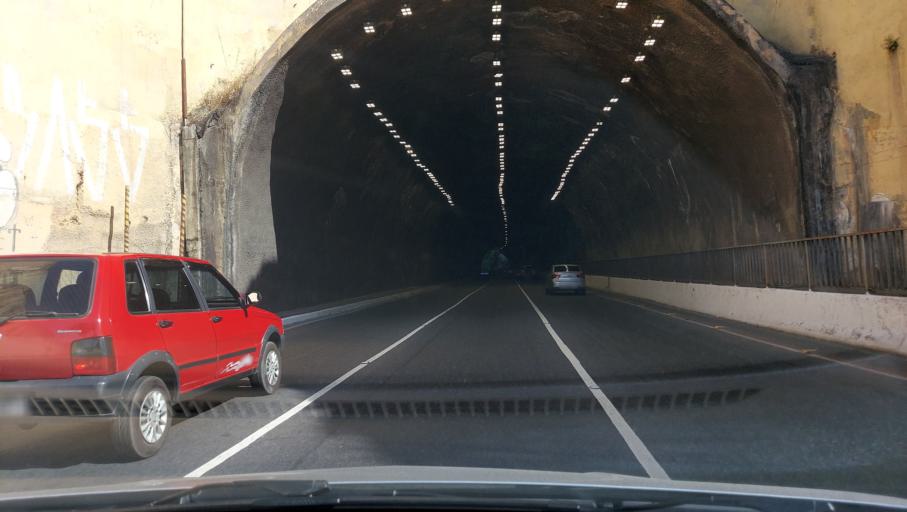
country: BR
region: Bahia
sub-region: Salvador
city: Salvador
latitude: -12.9564
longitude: -38.4676
